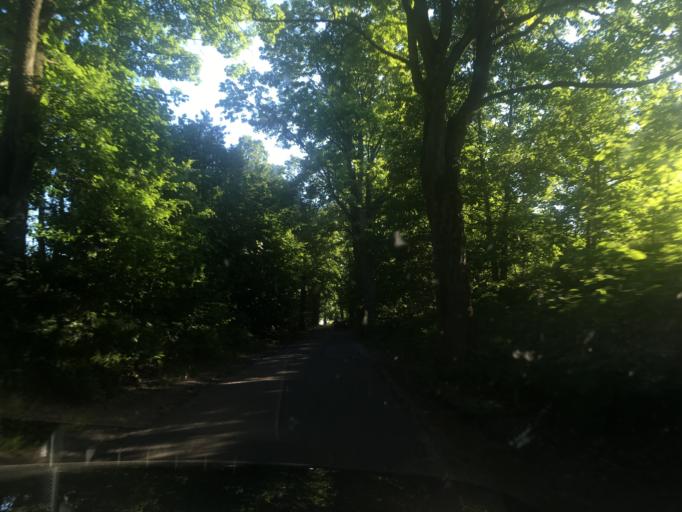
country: PL
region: Warmian-Masurian Voivodeship
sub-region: Powiat ostrodzki
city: Ostroda
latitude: 53.6810
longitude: 20.0536
